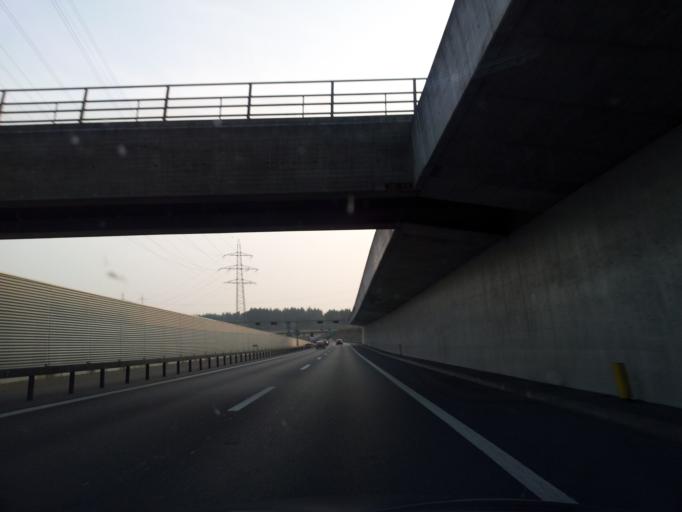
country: CH
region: Zurich
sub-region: Bezirk Affoltern
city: Hedingen
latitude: 47.2922
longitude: 8.4258
